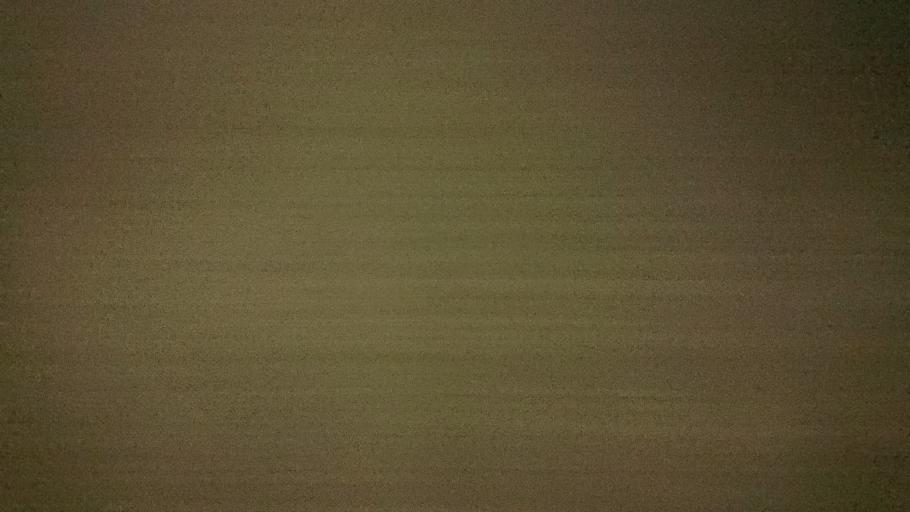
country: TW
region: Taiwan
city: Lugu
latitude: 23.8316
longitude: 120.8652
